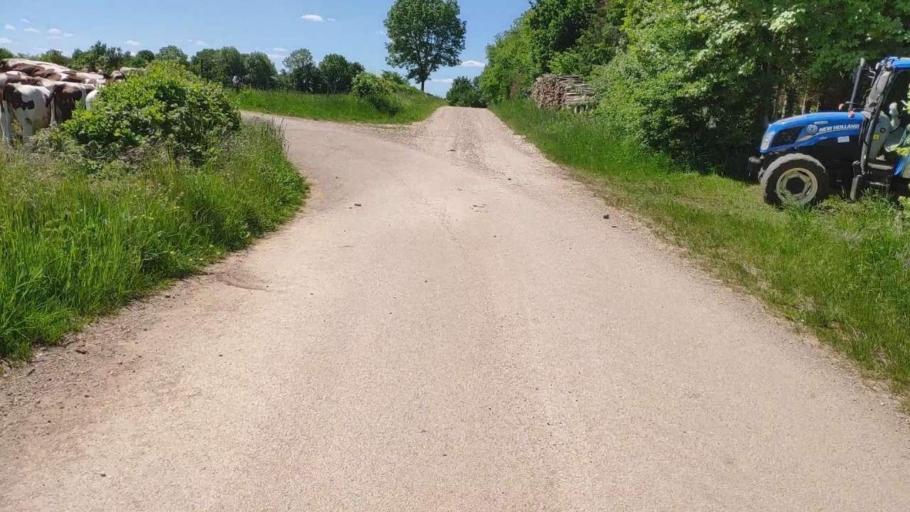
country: FR
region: Franche-Comte
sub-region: Departement du Jura
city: Poligny
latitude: 46.7309
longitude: 5.6965
